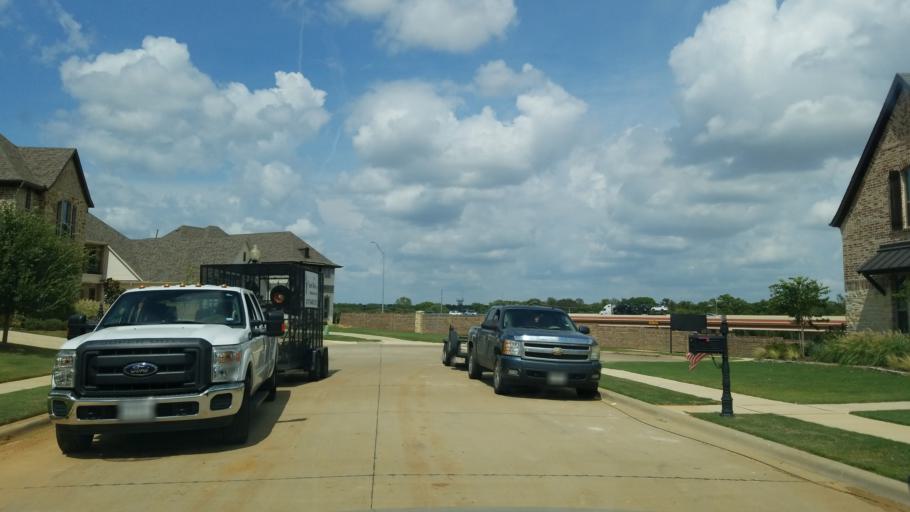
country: US
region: Texas
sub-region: Tarrant County
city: Grapevine
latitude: 32.8904
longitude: -97.0832
